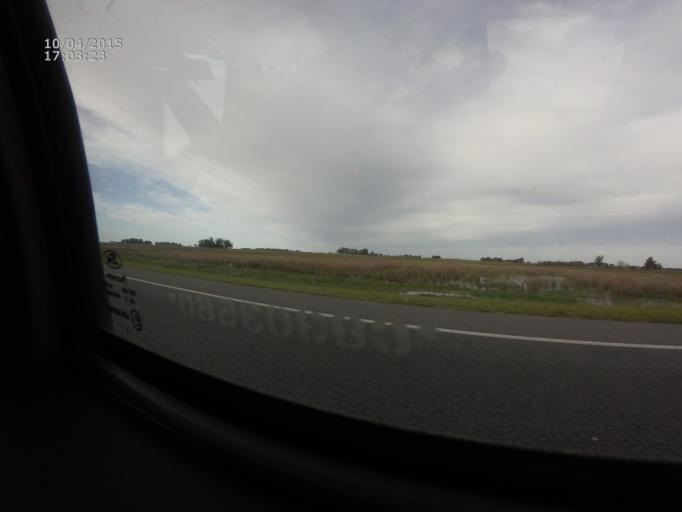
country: AR
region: Buenos Aires
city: Coronel Vidal
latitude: -37.4193
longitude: -57.7372
